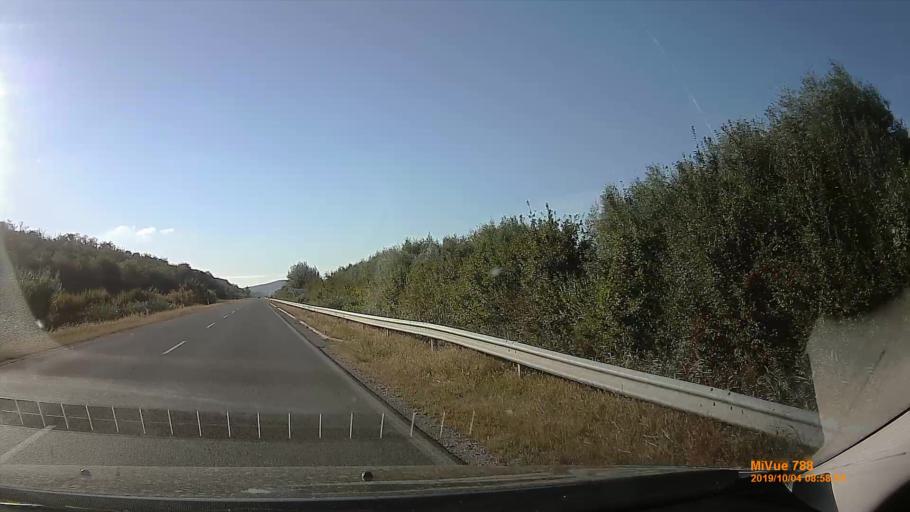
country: HU
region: Somogy
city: Balatonlelle
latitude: 46.7675
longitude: 17.7593
